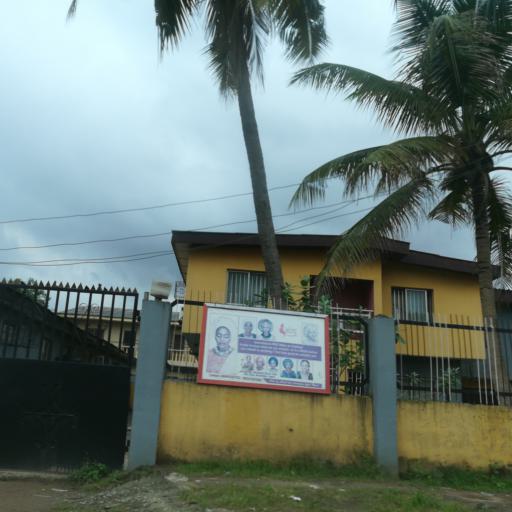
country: NG
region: Lagos
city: Agege
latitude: 6.6024
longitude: 3.3082
